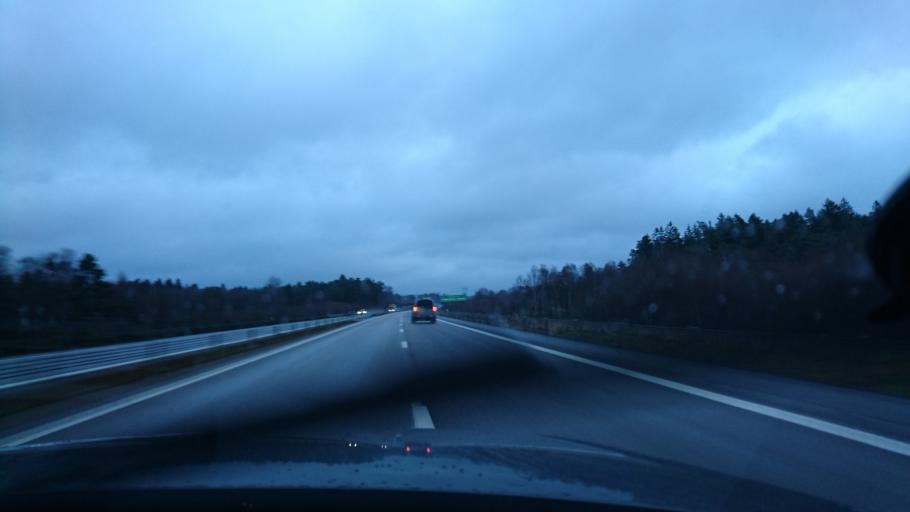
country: SE
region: Kronoberg
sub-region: Markaryds Kommun
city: Markaryd
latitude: 56.4426
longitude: 13.5899
